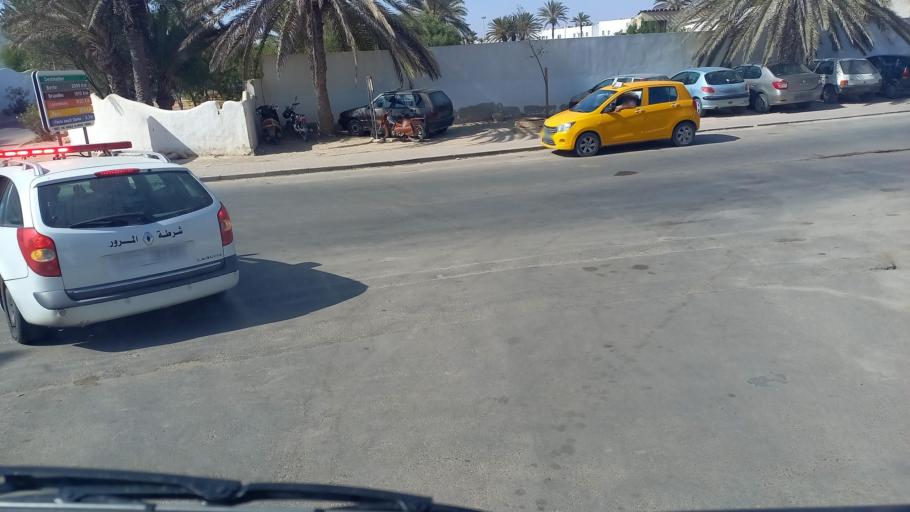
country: TN
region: Madanin
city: Midoun
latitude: 33.8510
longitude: 10.9889
